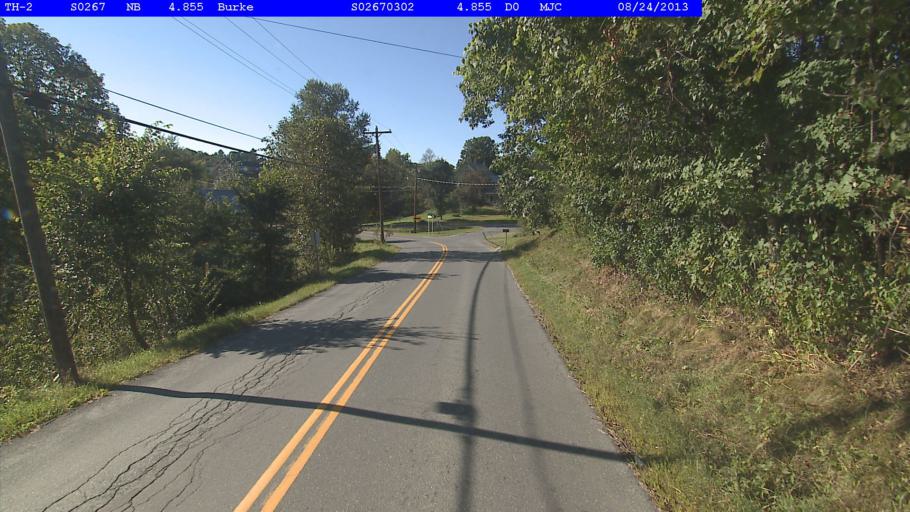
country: US
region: Vermont
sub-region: Caledonia County
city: Lyndonville
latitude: 44.6418
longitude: -71.9780
